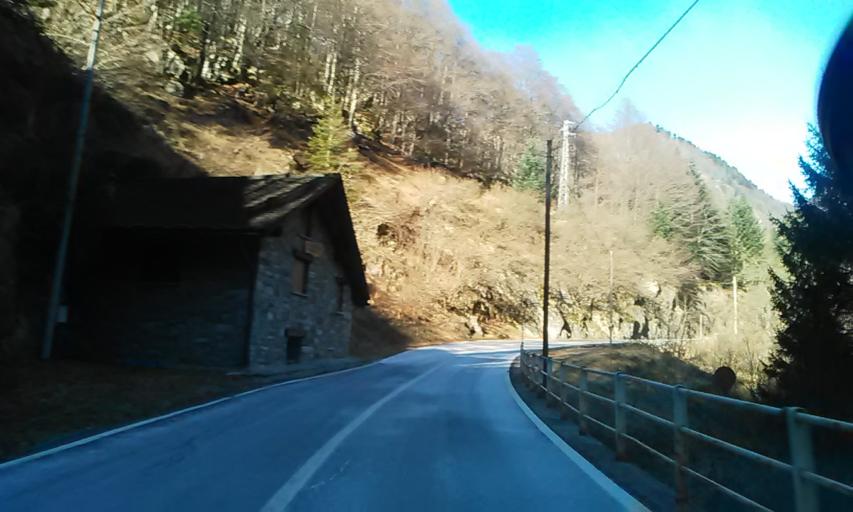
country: IT
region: Piedmont
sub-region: Provincia di Vercelli
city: Rimasco
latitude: 45.8745
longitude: 8.0706
